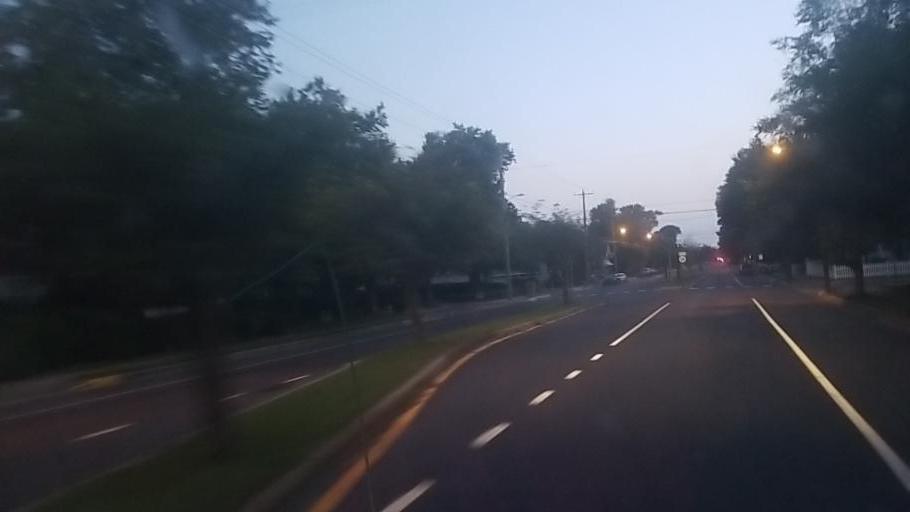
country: US
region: Delaware
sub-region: Sussex County
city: Rehoboth Beach
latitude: 38.7089
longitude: -75.0809
